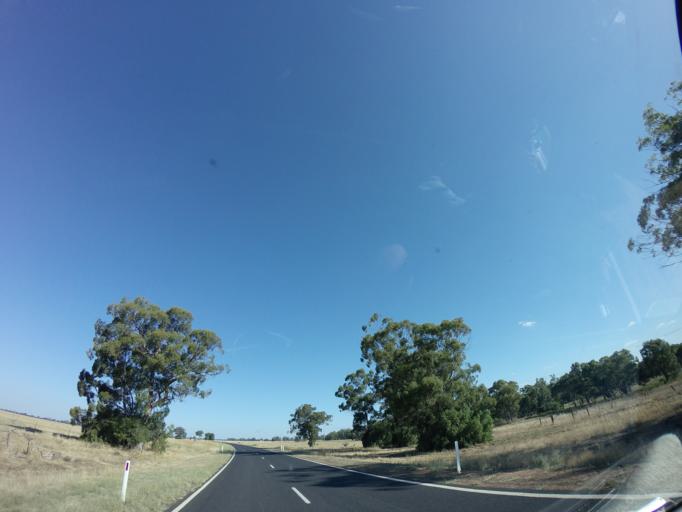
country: AU
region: New South Wales
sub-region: Gilgandra
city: Gilgandra
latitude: -31.6988
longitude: 148.5728
